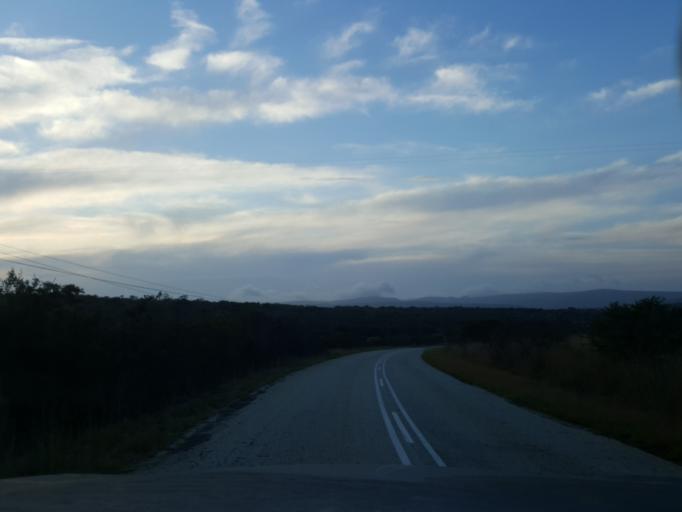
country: ZA
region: Eastern Cape
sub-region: Cacadu District Municipality
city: Grahamstown
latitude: -33.4201
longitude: 26.4737
